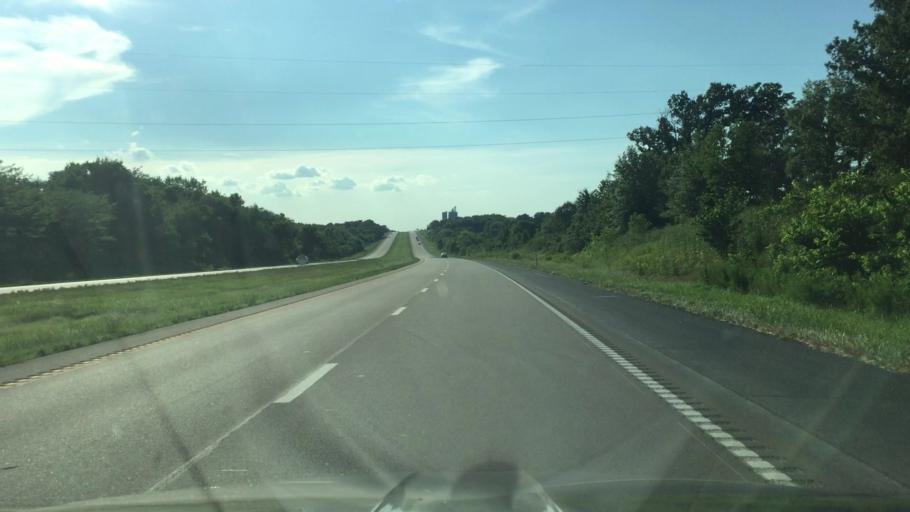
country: US
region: Missouri
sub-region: Pettis County
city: Sedalia
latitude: 38.7403
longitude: -93.3214
